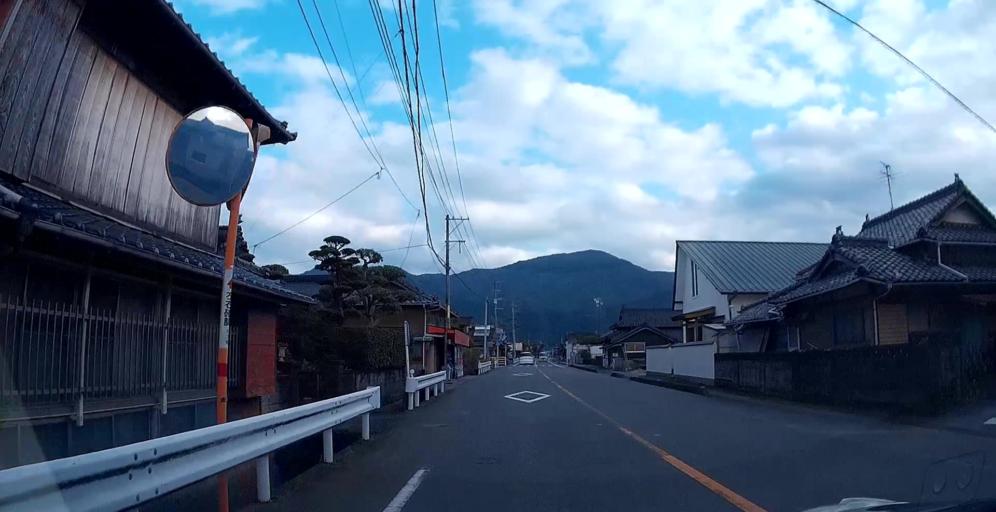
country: JP
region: Kumamoto
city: Yatsushiro
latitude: 32.5346
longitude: 130.6488
